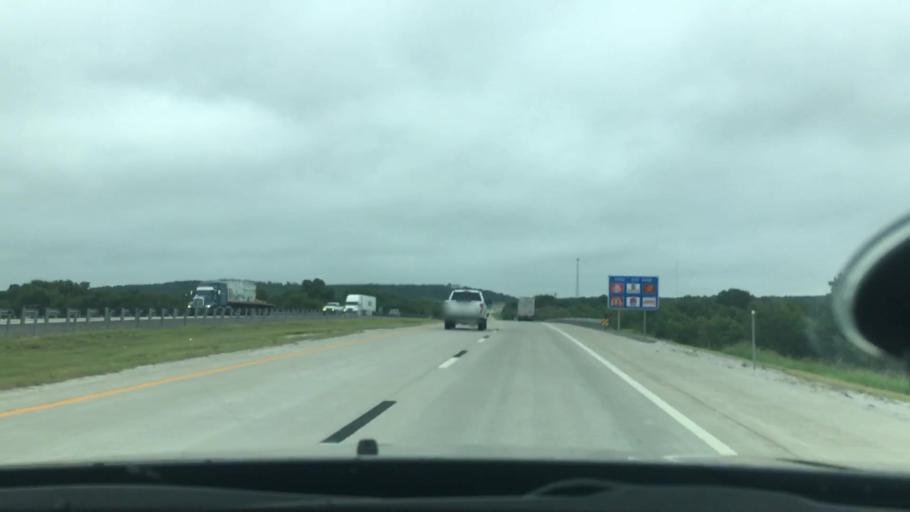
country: US
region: Oklahoma
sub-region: Okmulgee County
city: Henryetta
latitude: 35.4327
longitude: -95.9902
